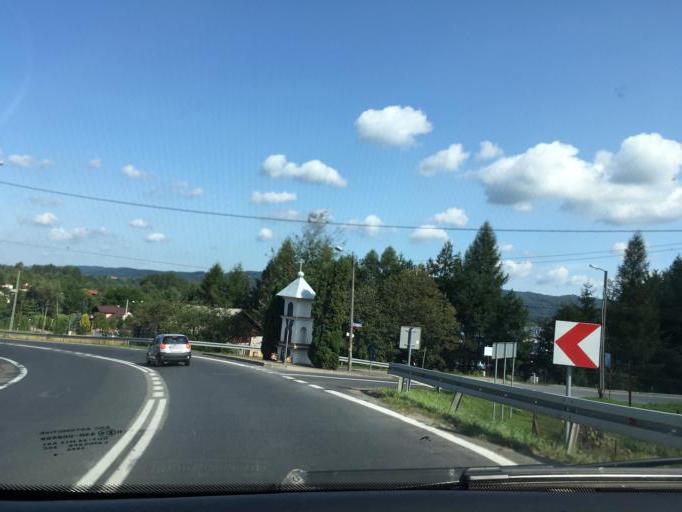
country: PL
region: Subcarpathian Voivodeship
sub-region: Powiat sanocki
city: Zagorz
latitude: 49.5120
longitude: 22.2715
